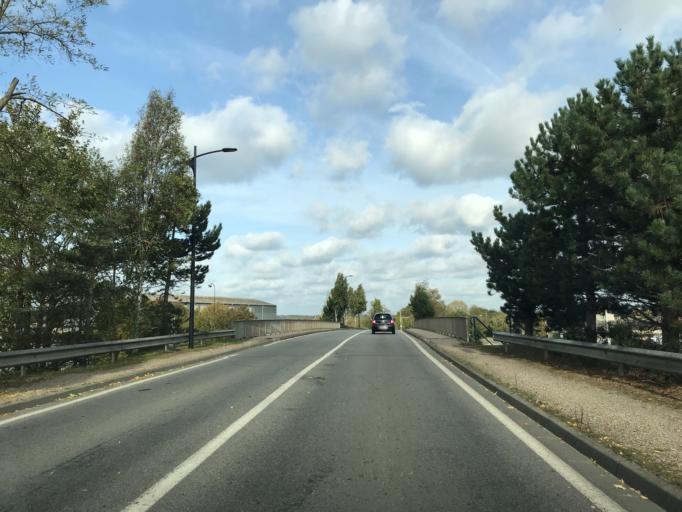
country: FR
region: Haute-Normandie
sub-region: Departement de l'Eure
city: Courcelles-sur-Seine
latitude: 49.1746
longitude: 1.3513
